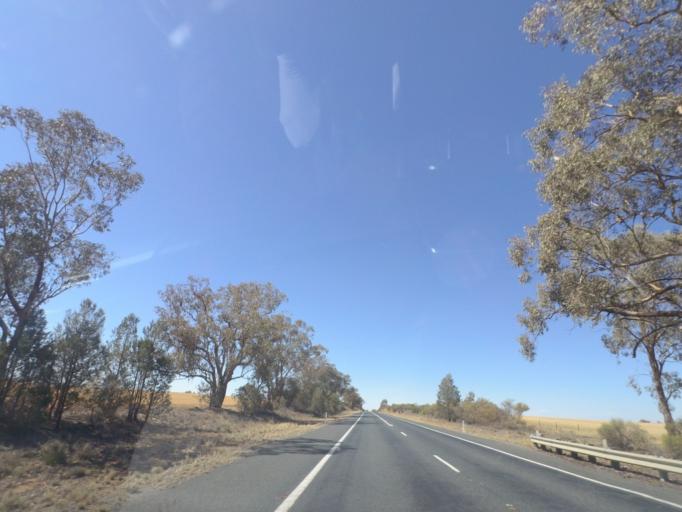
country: AU
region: New South Wales
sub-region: Bland
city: West Wyalong
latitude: -34.1773
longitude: 147.1140
